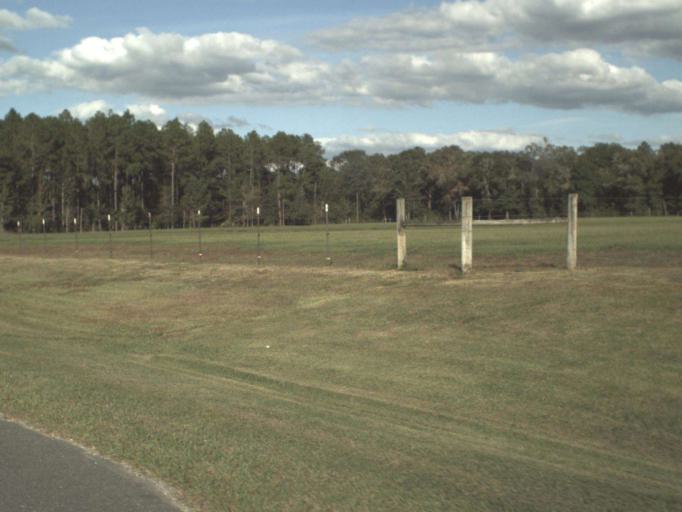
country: US
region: Florida
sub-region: Washington County
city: Chipley
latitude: 30.7279
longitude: -85.6121
